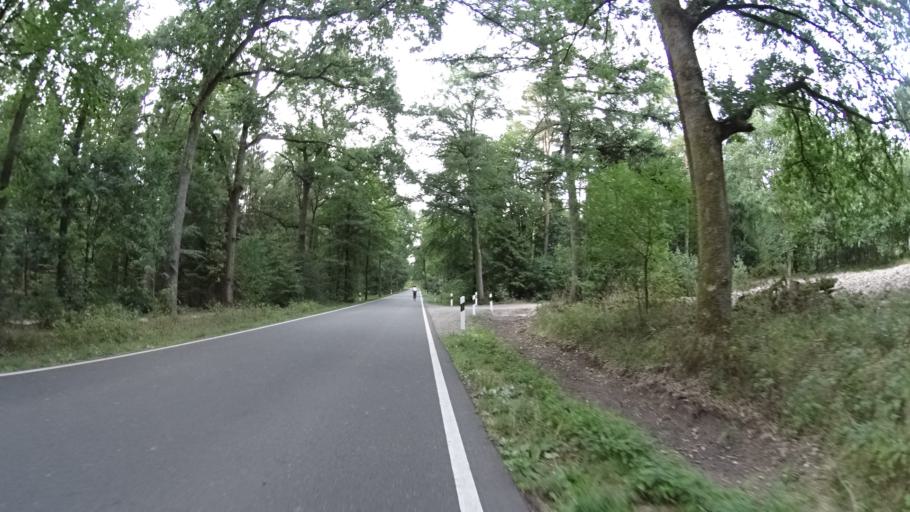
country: DE
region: Lower Saxony
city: Undeloh
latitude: 53.1668
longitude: 9.8949
